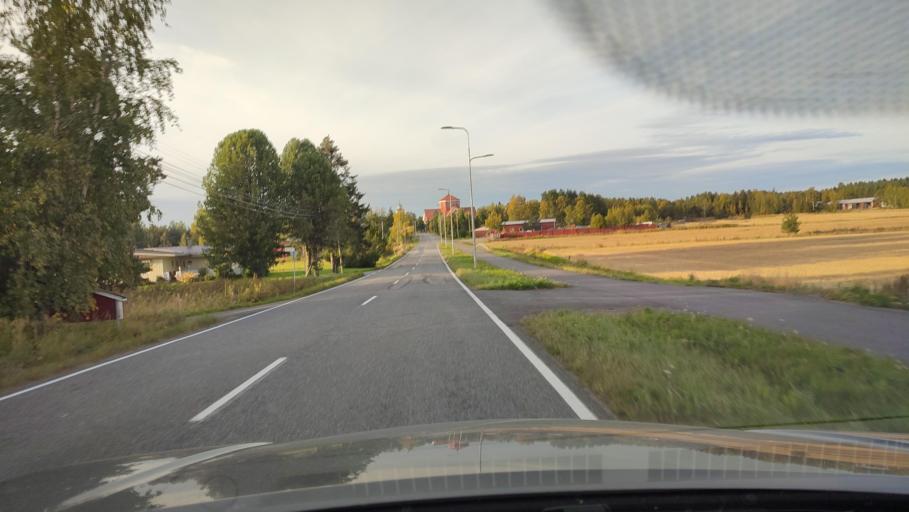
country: FI
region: Ostrobothnia
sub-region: Sydosterbotten
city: Kristinestad
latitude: 62.2411
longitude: 21.5209
